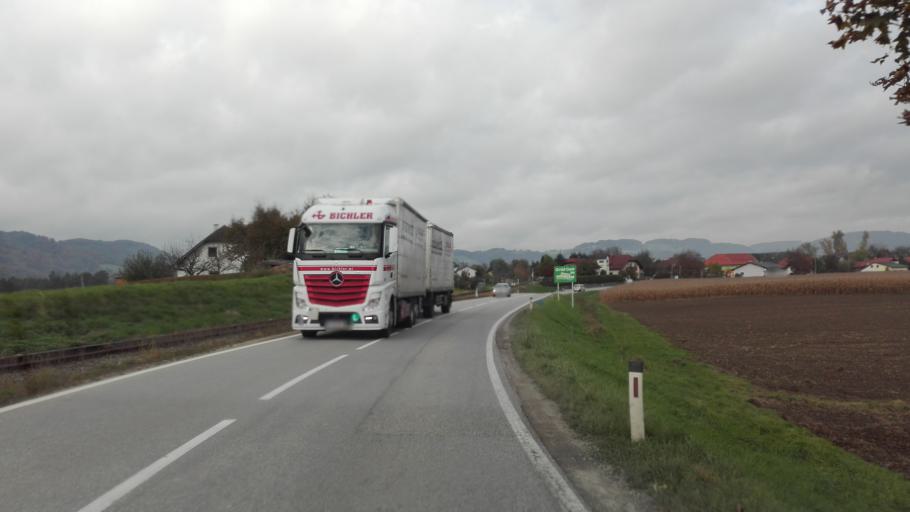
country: AT
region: Upper Austria
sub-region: Politischer Bezirk Urfahr-Umgebung
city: Feldkirchen an der Donau
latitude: 48.3471
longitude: 13.9967
